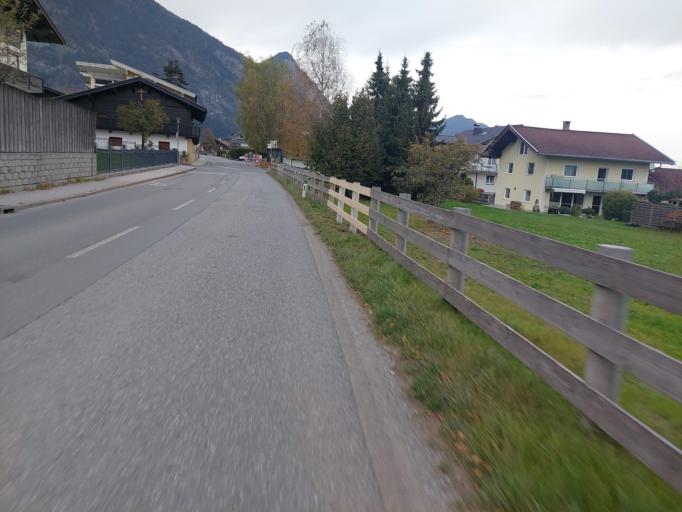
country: AT
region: Tyrol
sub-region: Politischer Bezirk Kufstein
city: Munster
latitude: 47.4132
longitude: 11.8309
